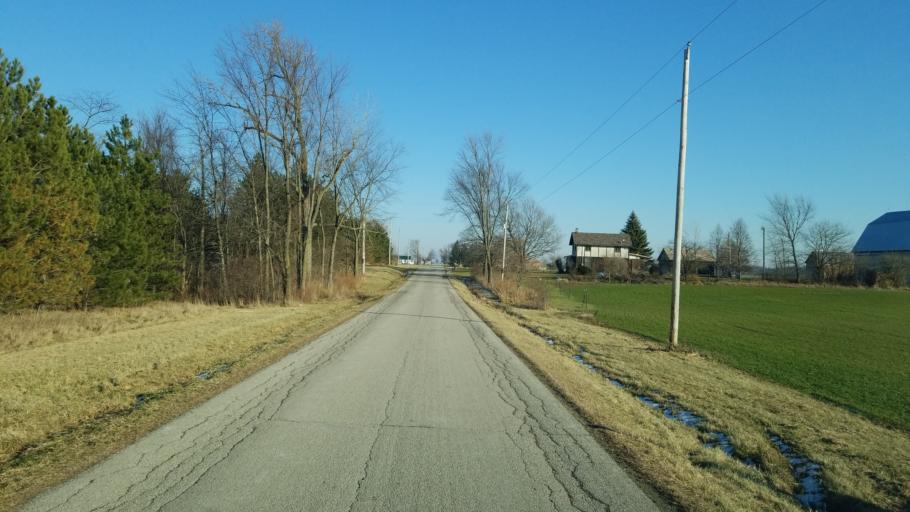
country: US
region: Ohio
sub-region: Sandusky County
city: Green Springs
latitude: 41.2273
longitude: -82.9981
